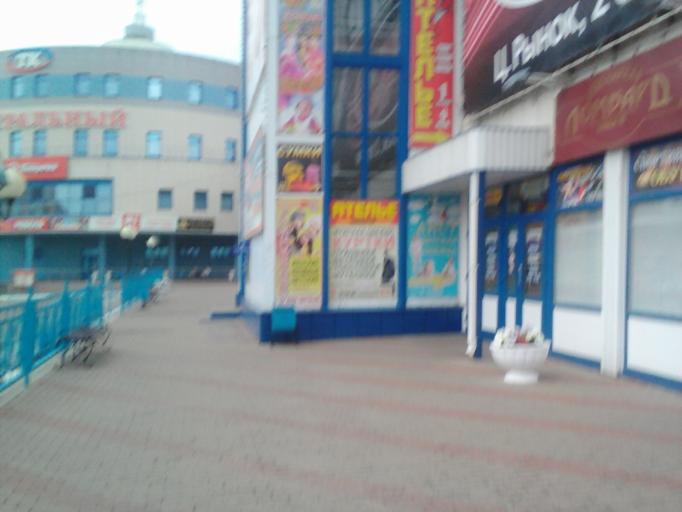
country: RU
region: Kursk
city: Kursk
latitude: 51.7285
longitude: 36.1836
